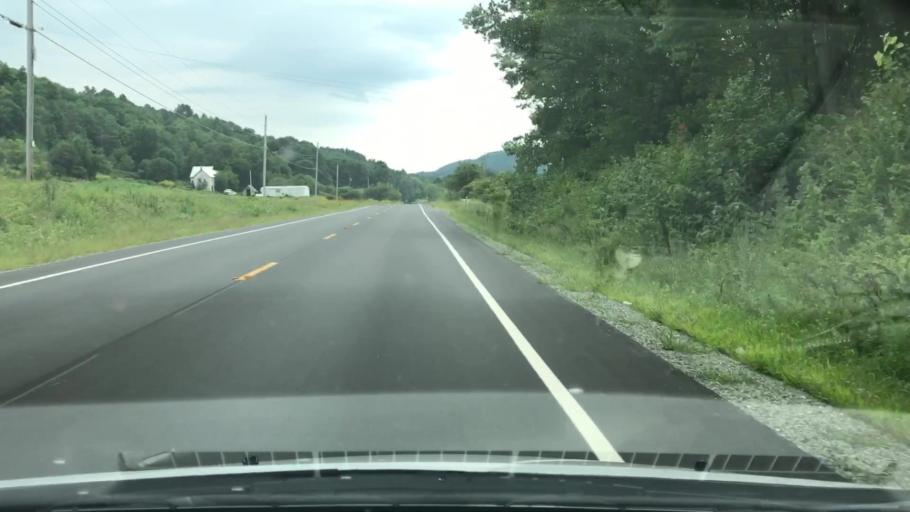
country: US
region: New Hampshire
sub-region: Grafton County
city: Orford
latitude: 43.8632
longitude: -72.1551
